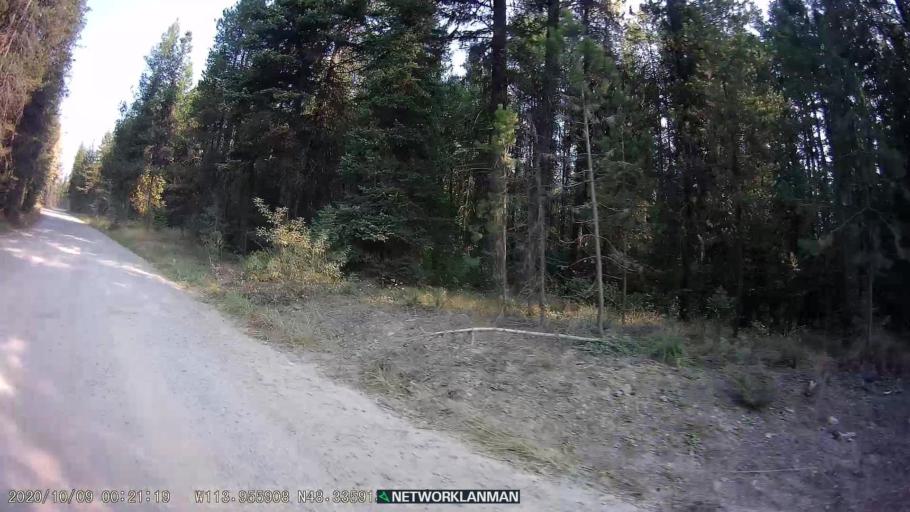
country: US
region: Montana
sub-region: Flathead County
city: Columbia Falls
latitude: 48.3375
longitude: -113.9571
